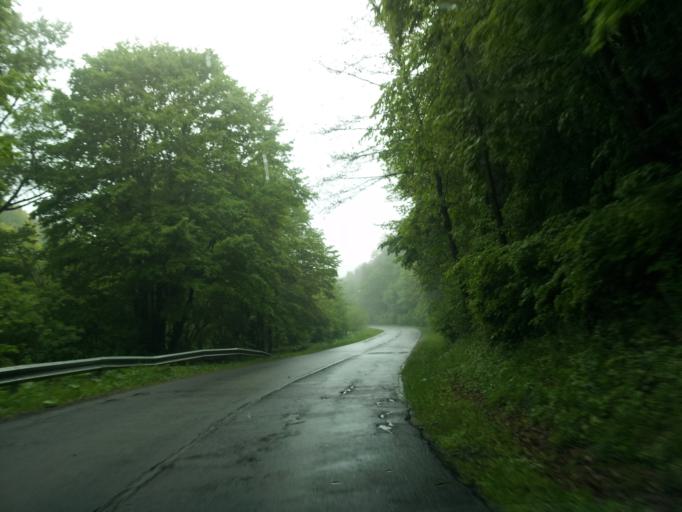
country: HU
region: Baranya
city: Komlo
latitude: 46.1963
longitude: 18.3052
